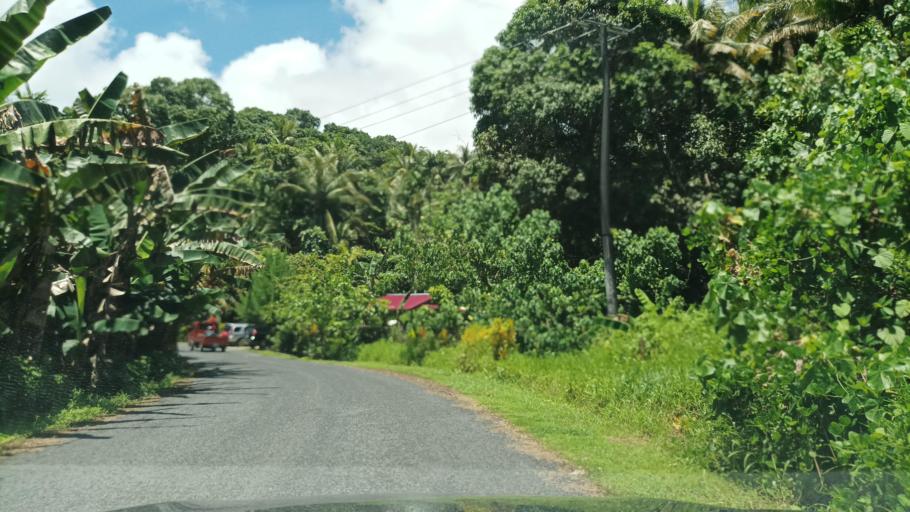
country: FM
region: Pohnpei
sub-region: Kolonia Municipality
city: Kolonia
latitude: 6.9268
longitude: 158.2800
